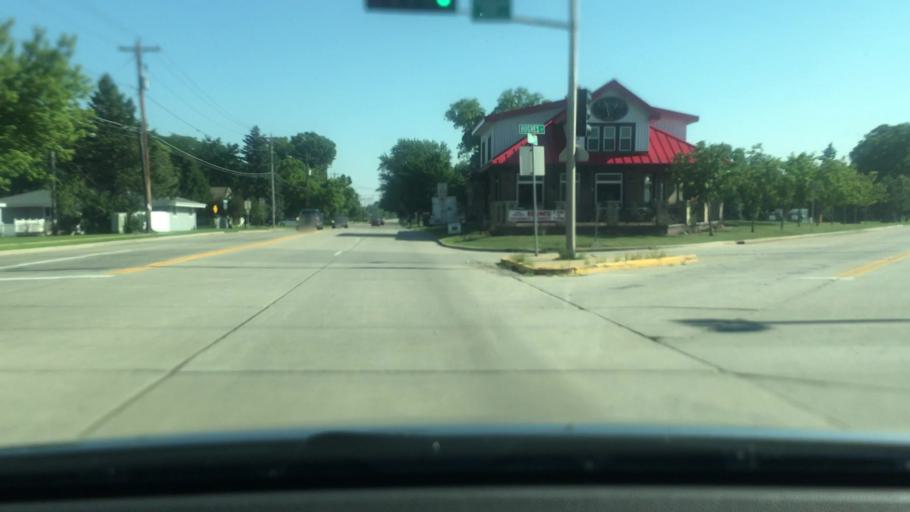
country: US
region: Wisconsin
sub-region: Winnebago County
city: Oshkosh
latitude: 43.9921
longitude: -88.5426
